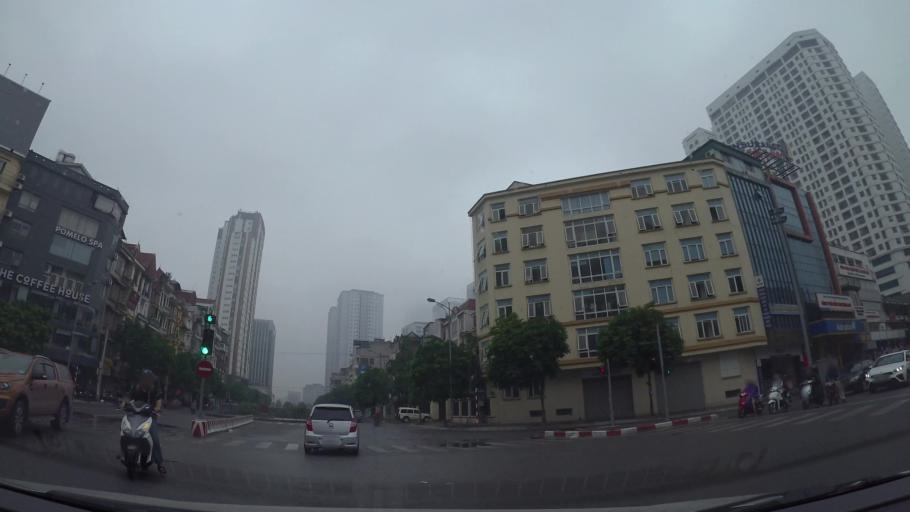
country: VN
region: Ha Noi
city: Cau Giay
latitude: 21.0192
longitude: 105.7926
